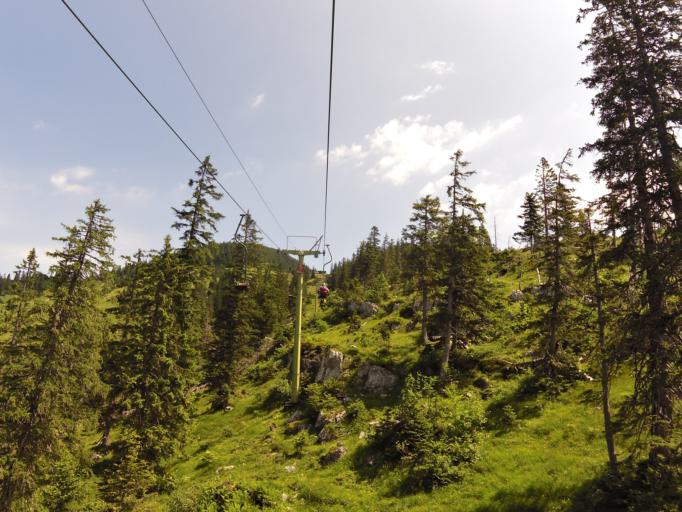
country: AT
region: Tyrol
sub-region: Politischer Bezirk Kitzbuhel
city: Waidring
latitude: 47.6669
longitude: 12.5966
